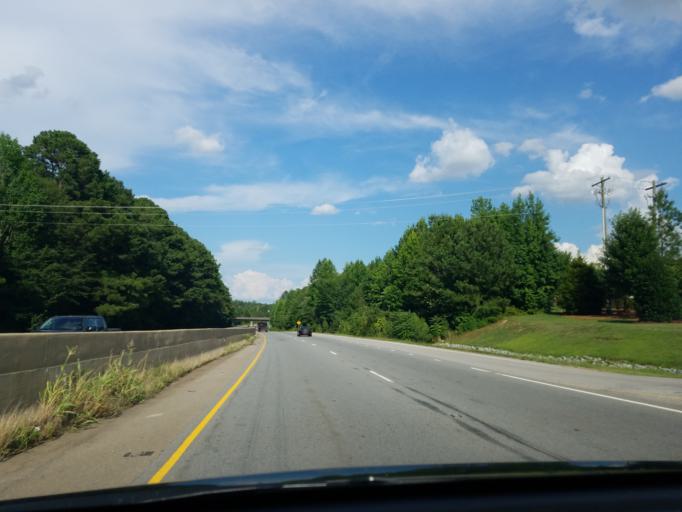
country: US
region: North Carolina
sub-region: Wake County
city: Apex
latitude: 35.7488
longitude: -78.8437
